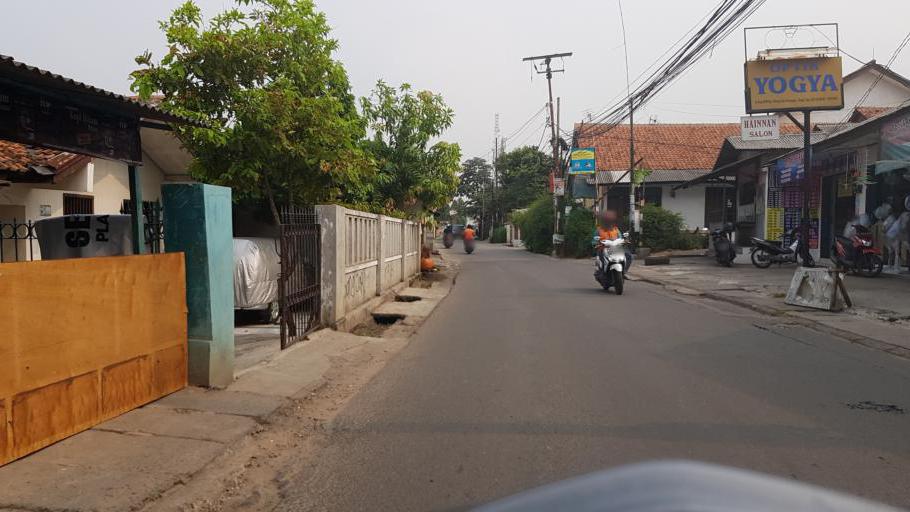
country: ID
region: West Java
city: Depok
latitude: -6.3568
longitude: 106.8429
